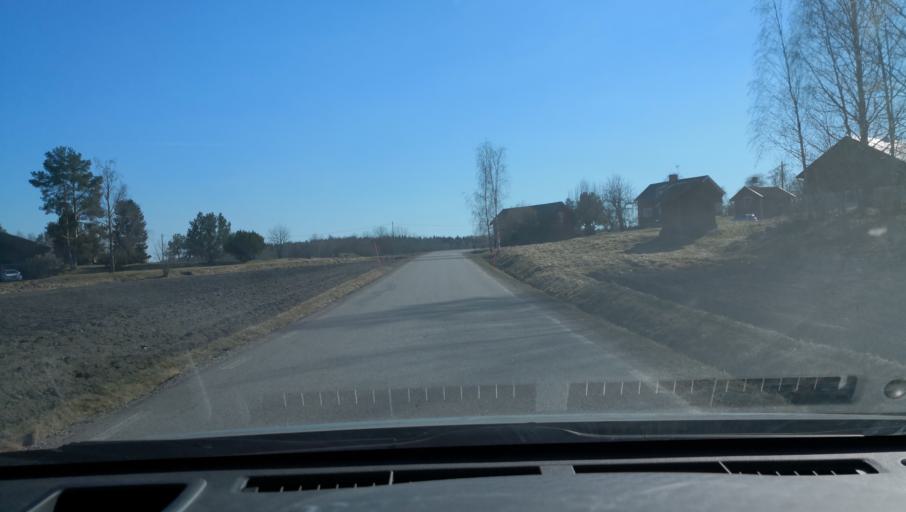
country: SE
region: Vaestmanland
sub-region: Sala Kommun
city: Sala
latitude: 60.0792
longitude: 16.4957
